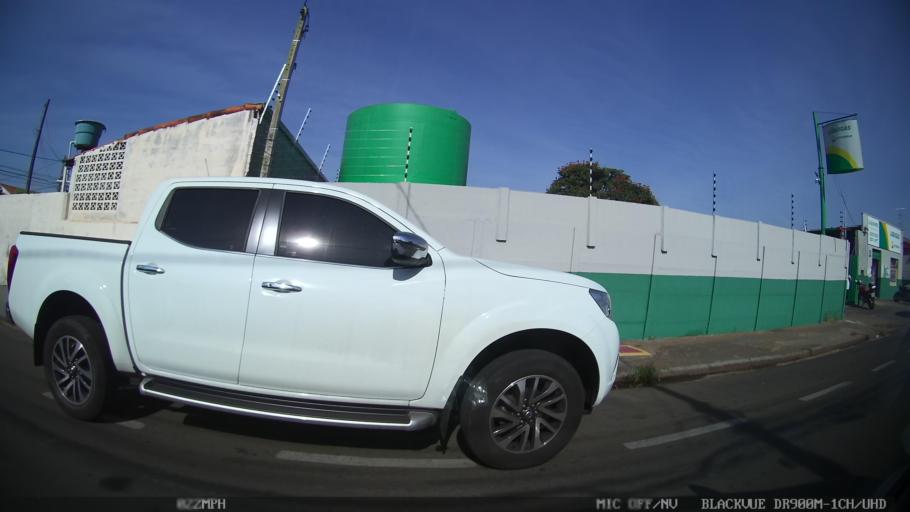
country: BR
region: Sao Paulo
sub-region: Sao Jose Do Rio Preto
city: Sao Jose do Rio Preto
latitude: -20.7945
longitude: -49.3830
